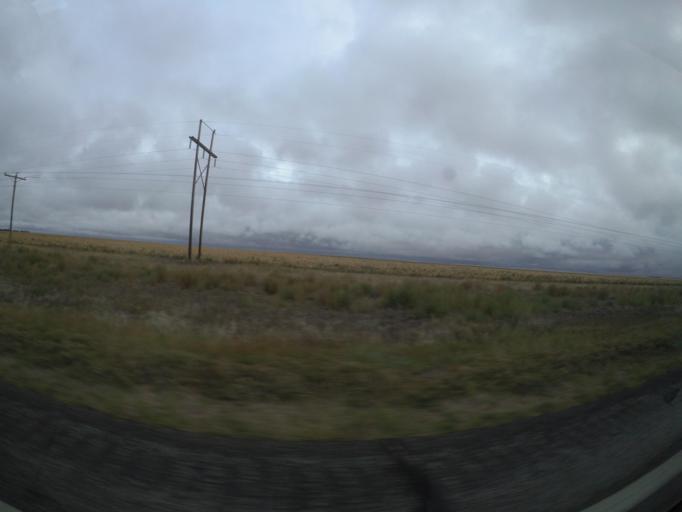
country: US
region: Colorado
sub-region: Washington County
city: Akron
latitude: 39.7397
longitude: -103.3195
